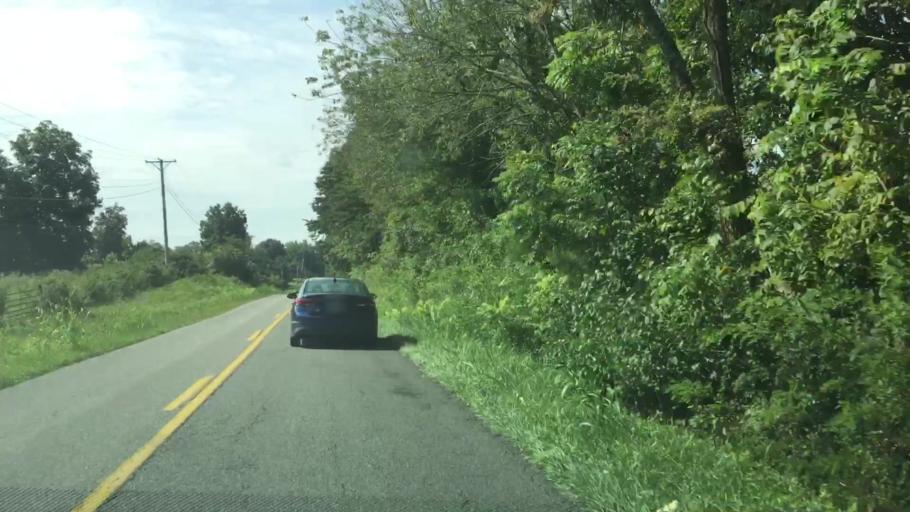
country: US
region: Tennessee
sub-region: Sullivan County
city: Fairmount
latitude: 36.6160
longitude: -82.0795
